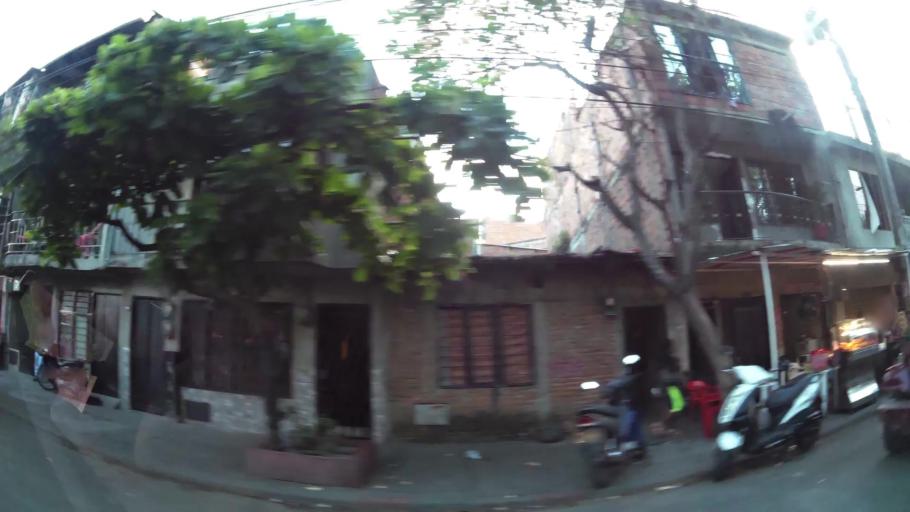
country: CO
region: Valle del Cauca
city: Cali
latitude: 3.4119
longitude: -76.5010
